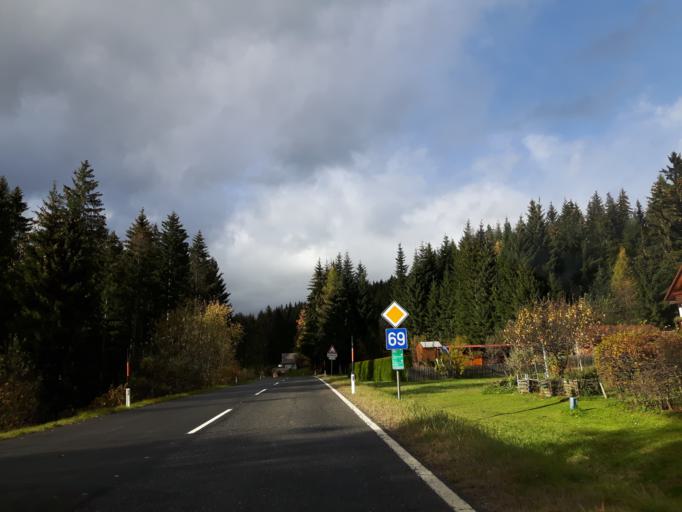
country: AT
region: Styria
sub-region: Politischer Bezirk Deutschlandsberg
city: Sankt Oswald ob Eibiswald
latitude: 46.7003
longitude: 15.1132
